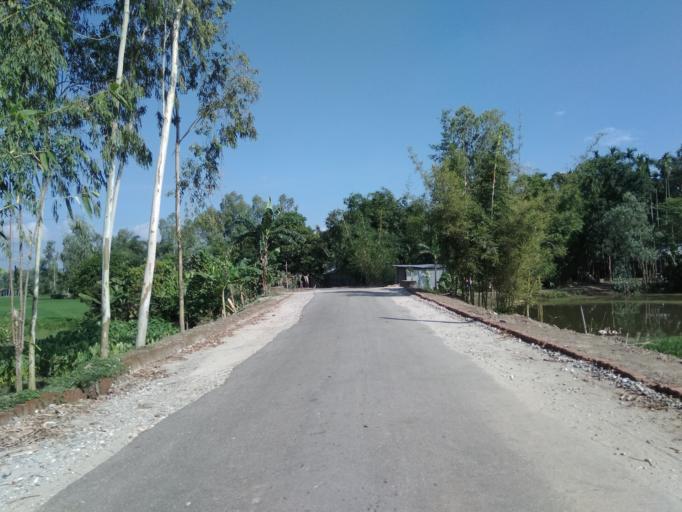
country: BD
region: Rangpur Division
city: Panchagarh
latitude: 26.2560
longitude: 88.6154
